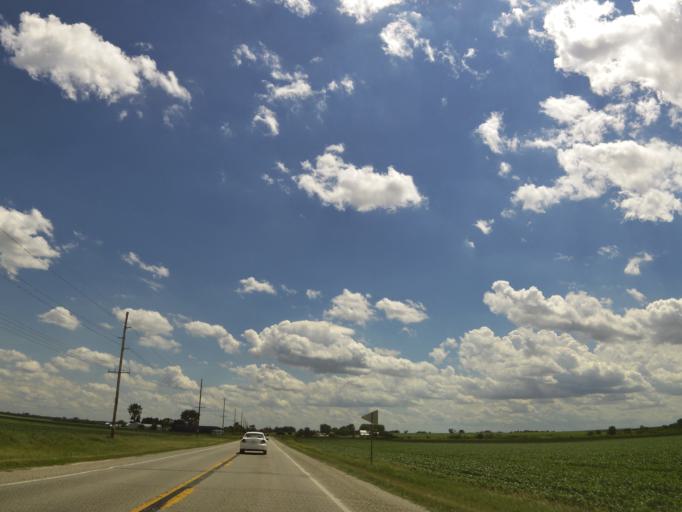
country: US
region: Iowa
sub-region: Buchanan County
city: Independence
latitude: 42.4181
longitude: -91.8899
